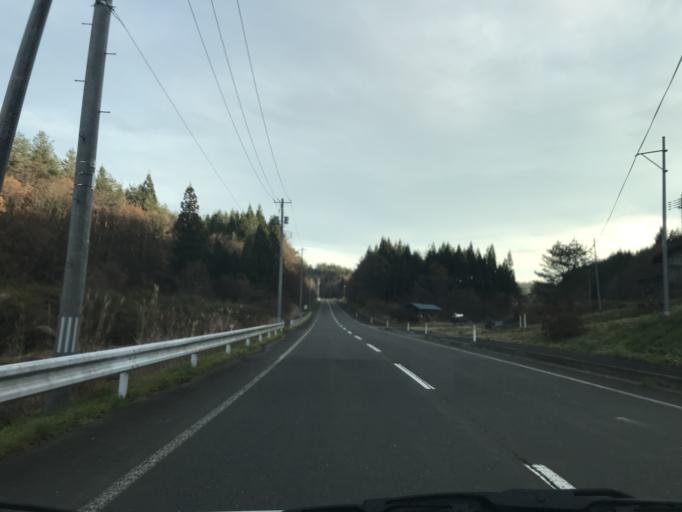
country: JP
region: Iwate
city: Ichinoseki
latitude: 38.9906
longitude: 141.0664
